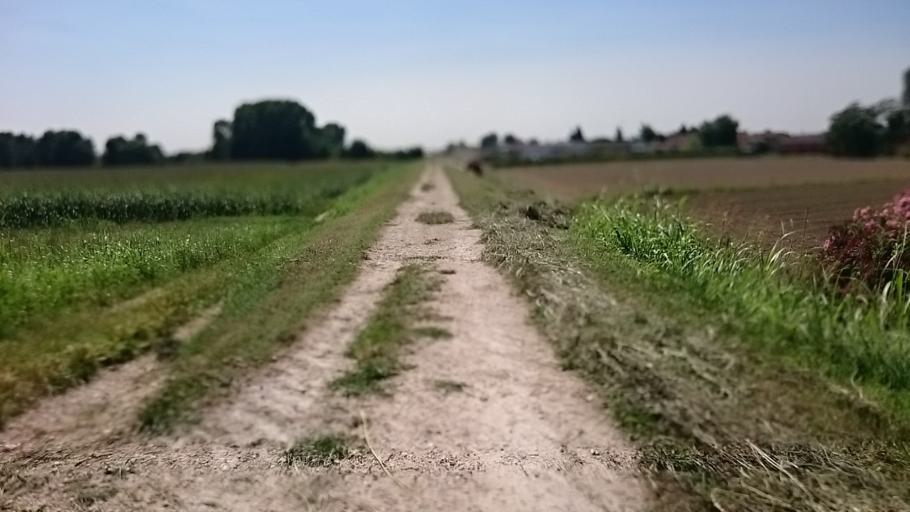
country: IT
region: Veneto
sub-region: Provincia di Padova
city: Saccolongo
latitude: 45.4026
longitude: 11.7577
